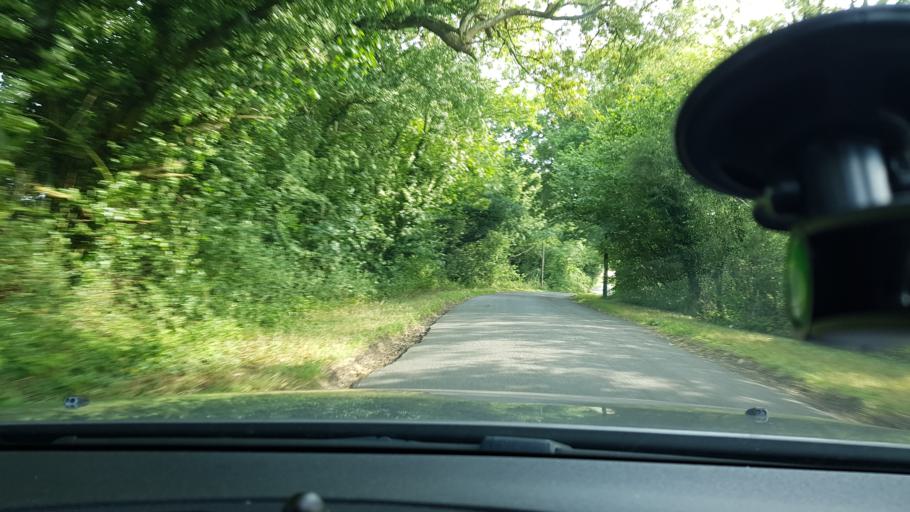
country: GB
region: England
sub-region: Wiltshire
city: Chilton Foliat
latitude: 51.4672
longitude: -1.5505
